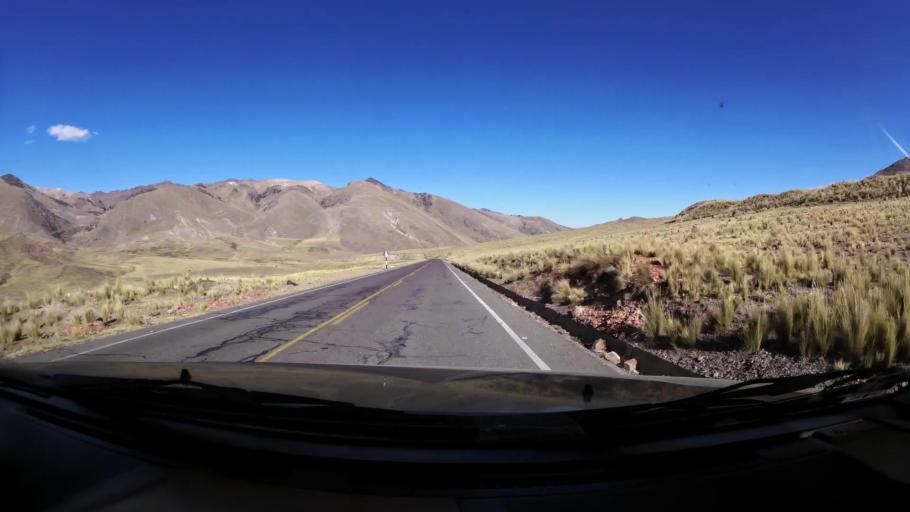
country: PE
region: Huancavelica
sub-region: Huaytara
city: Pilpichaca
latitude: -13.3619
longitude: -74.9539
